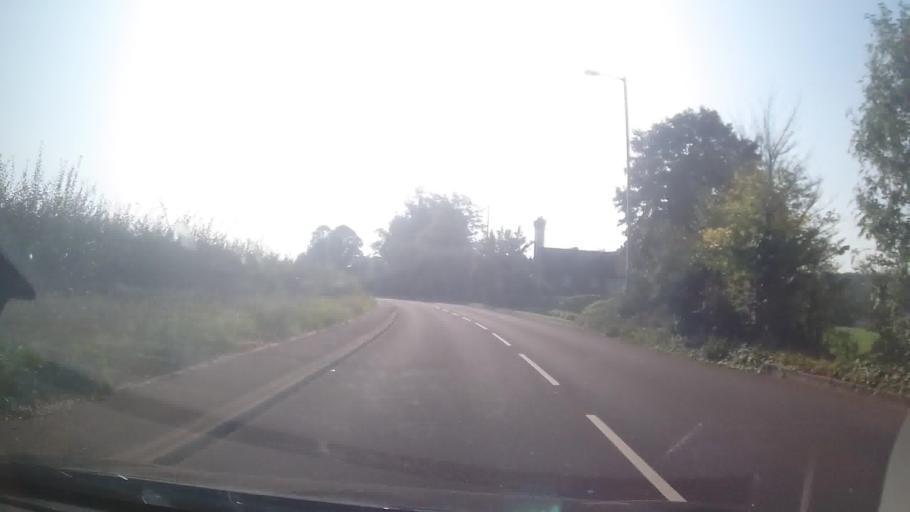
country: GB
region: England
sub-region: Shropshire
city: Bridgnorth
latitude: 52.5247
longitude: -2.4103
